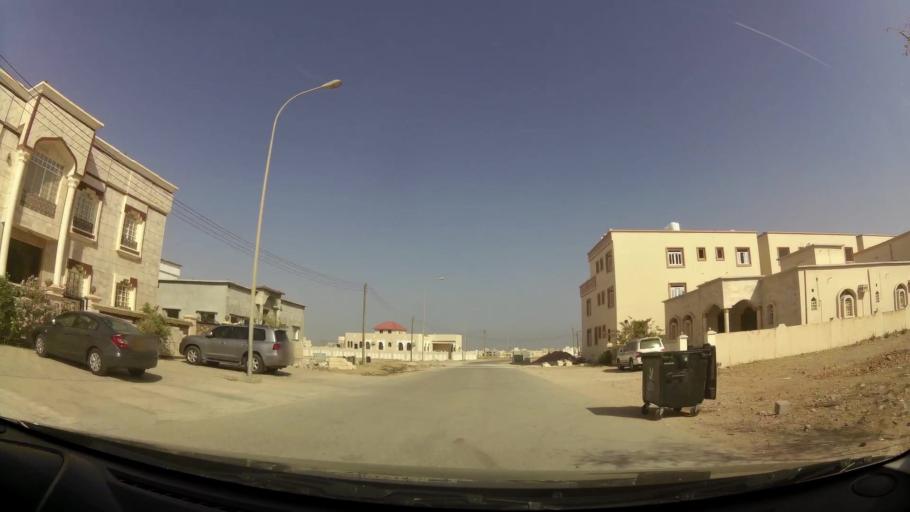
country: OM
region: Zufar
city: Salalah
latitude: 17.0126
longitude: 54.0069
